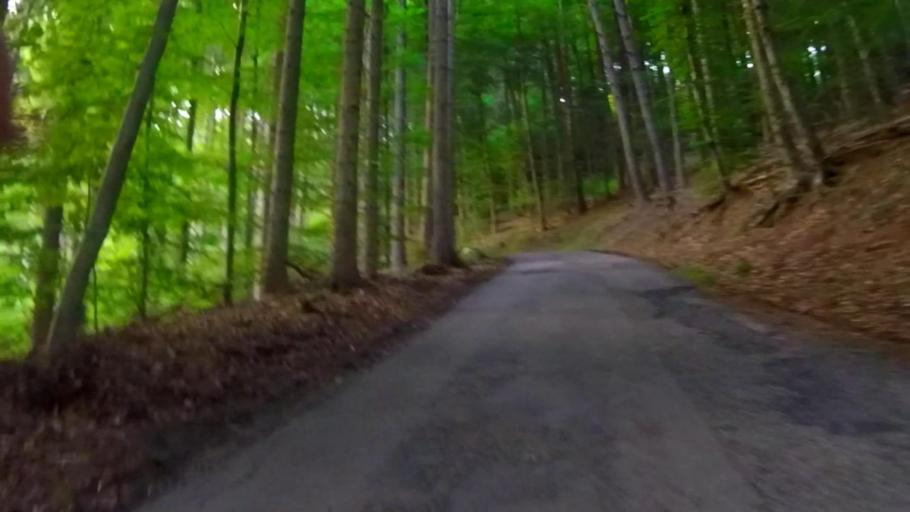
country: DE
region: Baden-Wuerttemberg
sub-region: Regierungsbezirk Stuttgart
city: Oppenweiler
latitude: 49.0083
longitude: 9.4419
